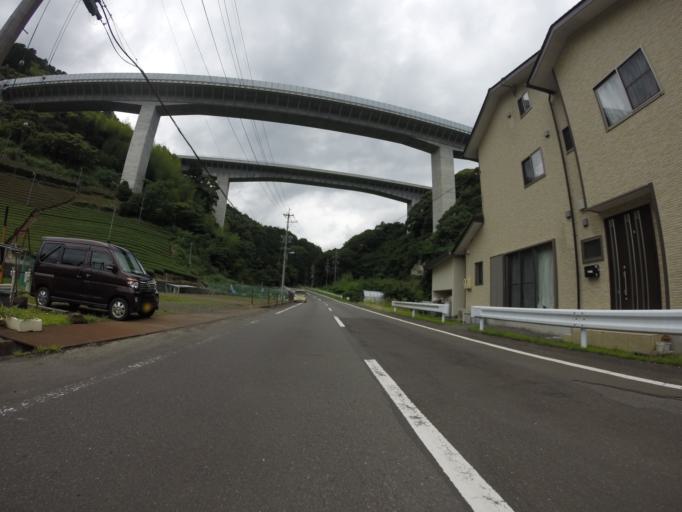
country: JP
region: Shizuoka
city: Shizuoka-shi
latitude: 35.0078
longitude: 138.3160
